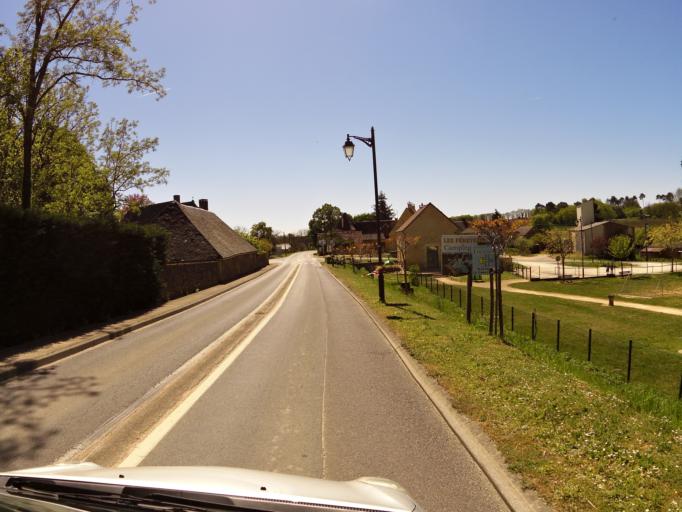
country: FR
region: Aquitaine
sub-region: Departement de la Dordogne
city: Eyvigues-et-Eybenes
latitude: 44.9640
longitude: 1.2745
